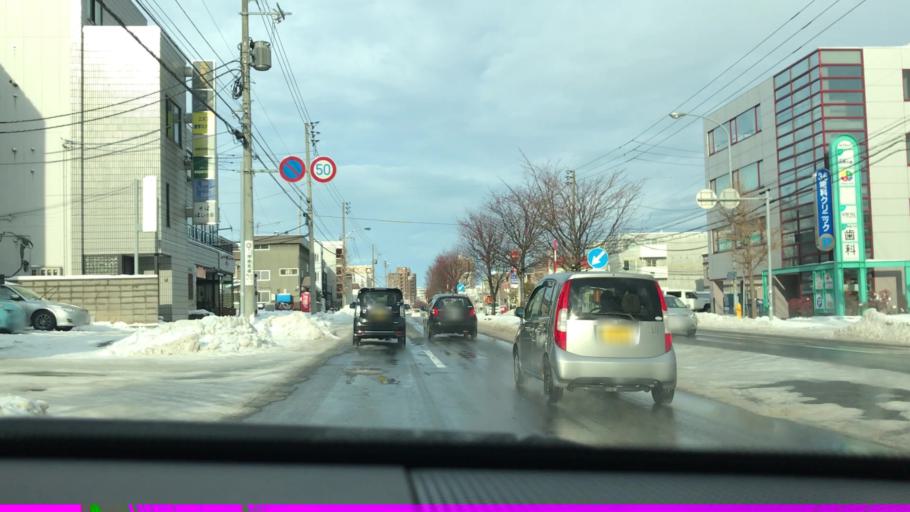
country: JP
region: Hokkaido
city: Sapporo
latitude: 43.0834
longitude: 141.2870
